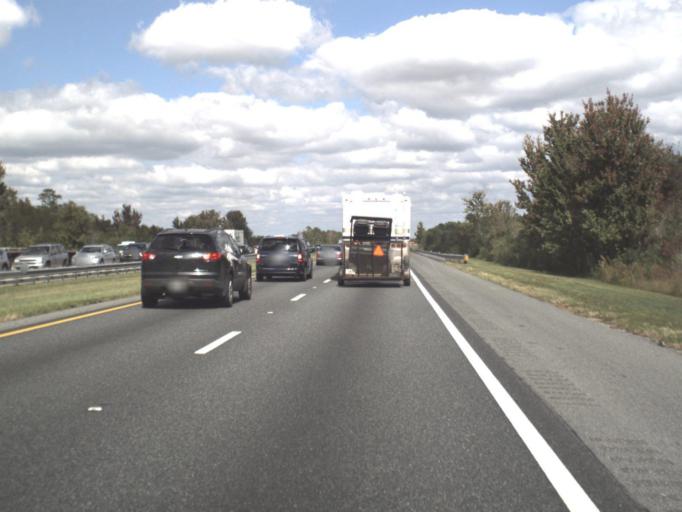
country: US
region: Florida
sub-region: Orange County
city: Southchase
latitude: 28.3756
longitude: -81.3903
